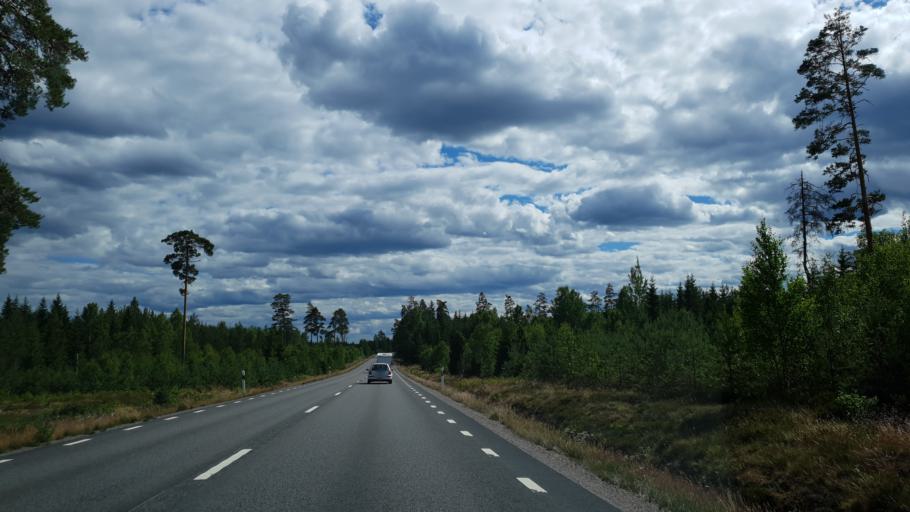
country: SE
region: Kronoberg
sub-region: Lessebo Kommun
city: Lessebo
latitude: 56.8094
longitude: 15.4118
